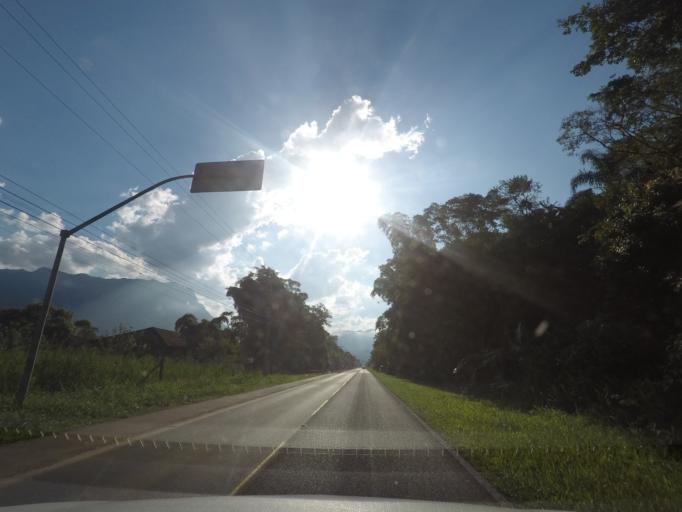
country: BR
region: Parana
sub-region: Antonina
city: Antonina
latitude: -25.4635
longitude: -48.8509
